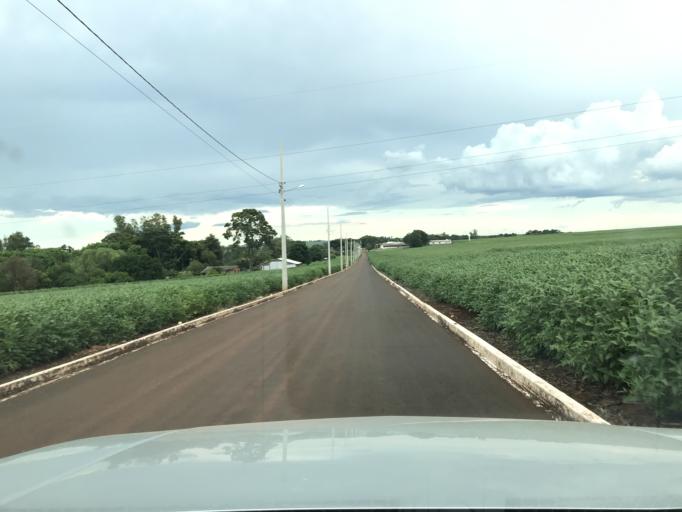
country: BR
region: Parana
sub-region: Palotina
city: Palotina
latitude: -24.2837
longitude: -53.7938
